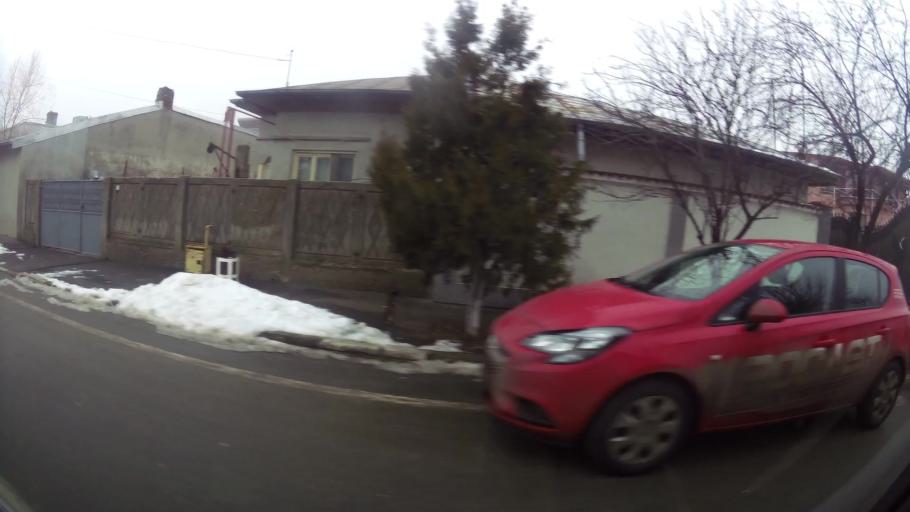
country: RO
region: Ilfov
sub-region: Comuna Chiajna
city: Chiajna
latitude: 44.4615
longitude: 25.9805
